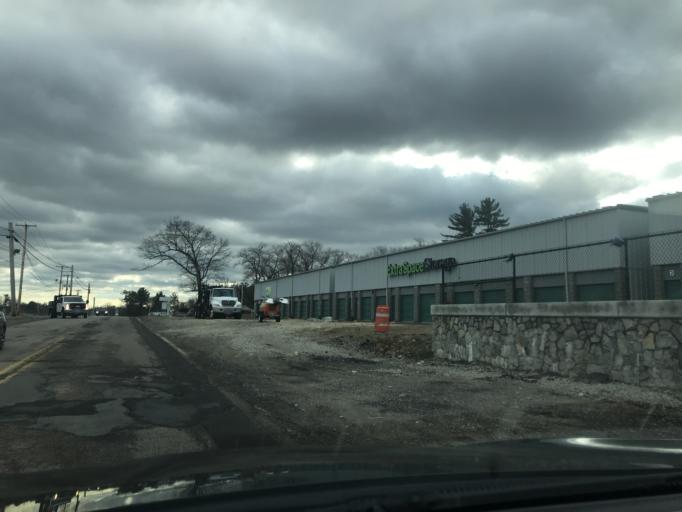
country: US
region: Massachusetts
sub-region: Plymouth County
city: Abington
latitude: 42.1429
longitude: -70.9533
